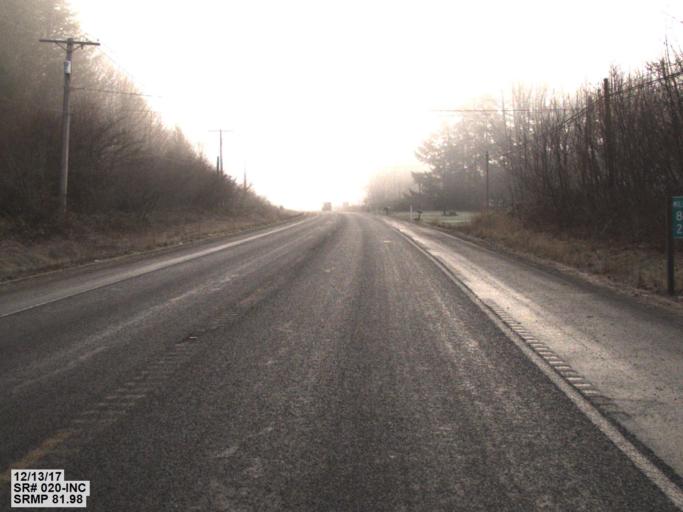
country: US
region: Washington
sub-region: Skagit County
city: Sedro-Woolley
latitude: 48.5308
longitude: -121.8938
